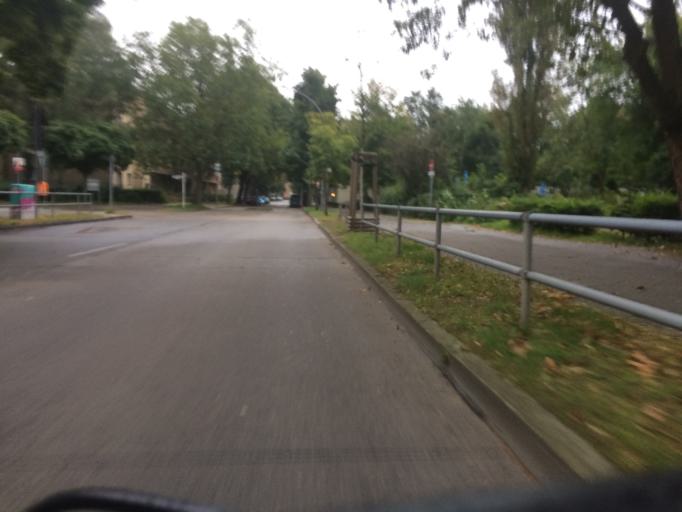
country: DE
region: Berlin
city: Wilhelmsruh
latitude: 52.5713
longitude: 13.3681
